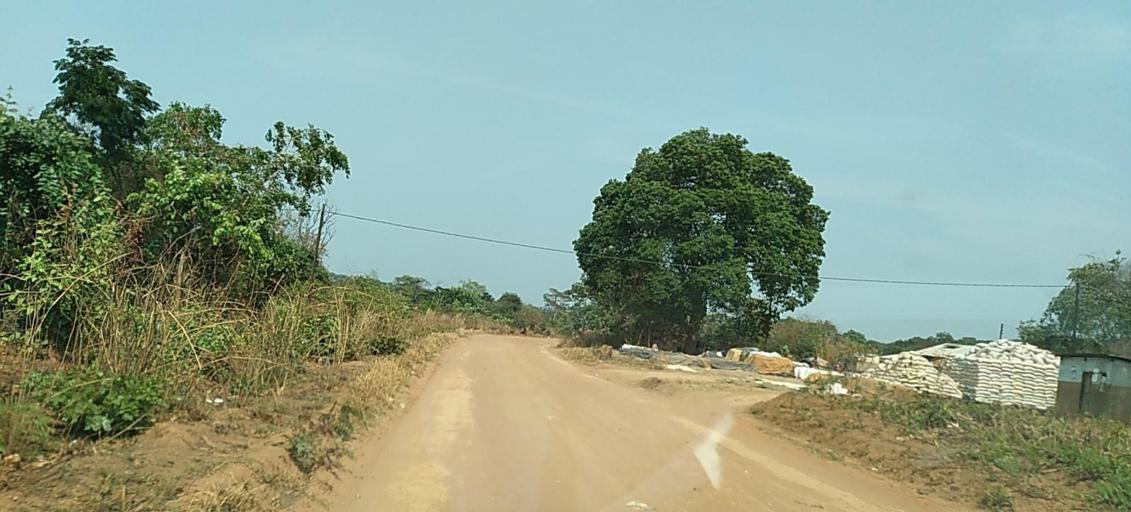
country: ZM
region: Copperbelt
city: Chililabombwe
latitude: -12.3395
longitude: 27.7180
